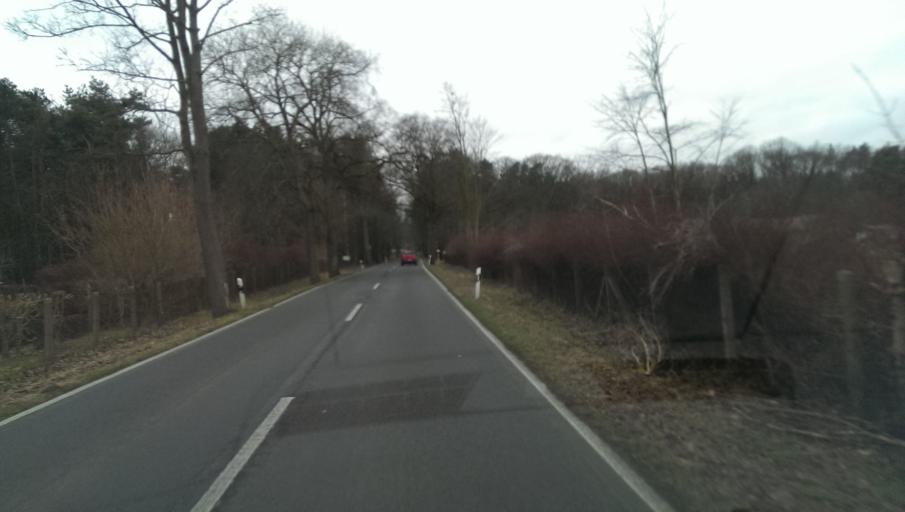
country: DE
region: Brandenburg
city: Ludwigsfelde
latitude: 52.2828
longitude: 13.2972
